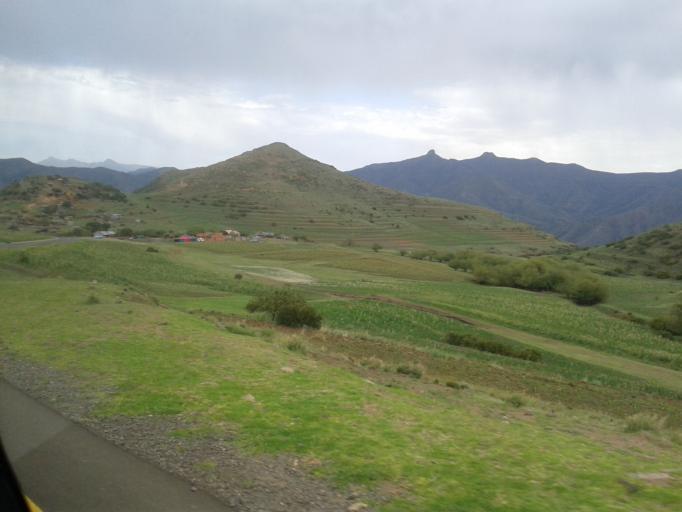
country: LS
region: Maseru
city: Nako
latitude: -29.6570
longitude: 27.8581
